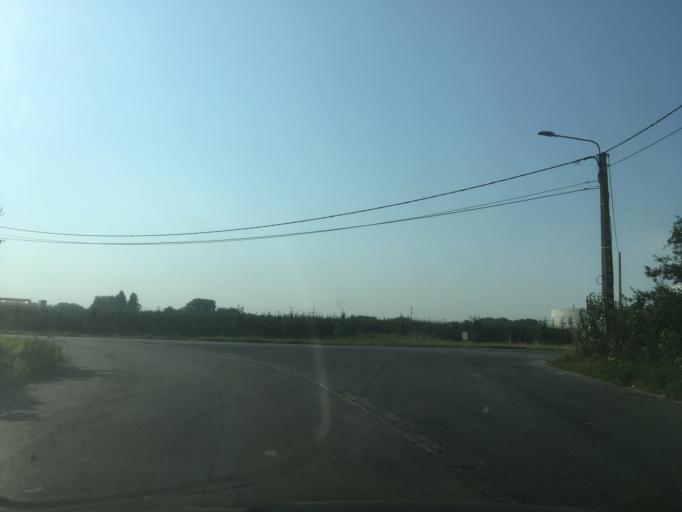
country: BE
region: Flanders
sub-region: Provincie West-Vlaanderen
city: Oostrozebeke
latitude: 50.9094
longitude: 3.3425
